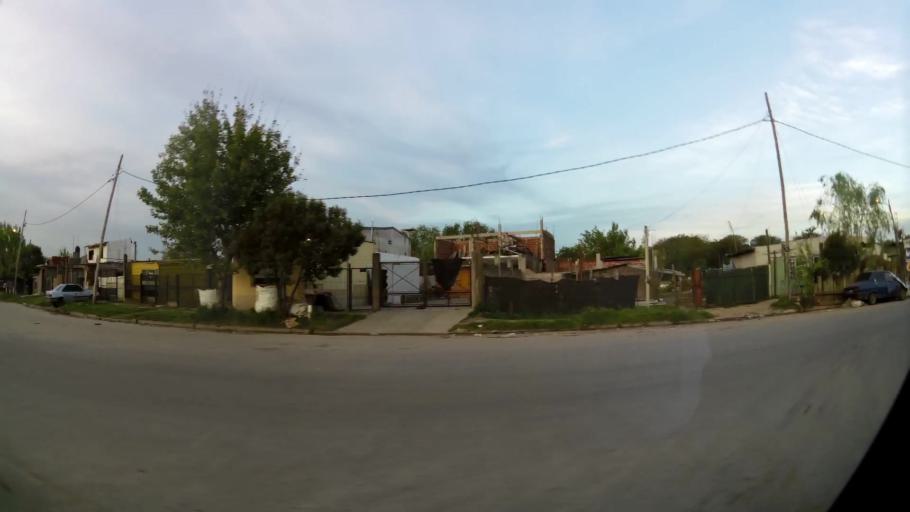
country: AR
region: Buenos Aires
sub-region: Partido de Almirante Brown
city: Adrogue
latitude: -34.8022
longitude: -58.3005
